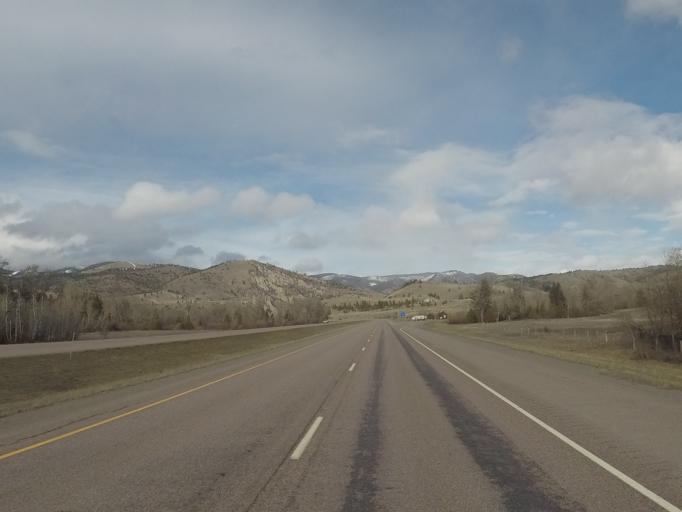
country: US
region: Montana
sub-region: Granite County
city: Philipsburg
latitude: 46.7012
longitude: -113.3458
